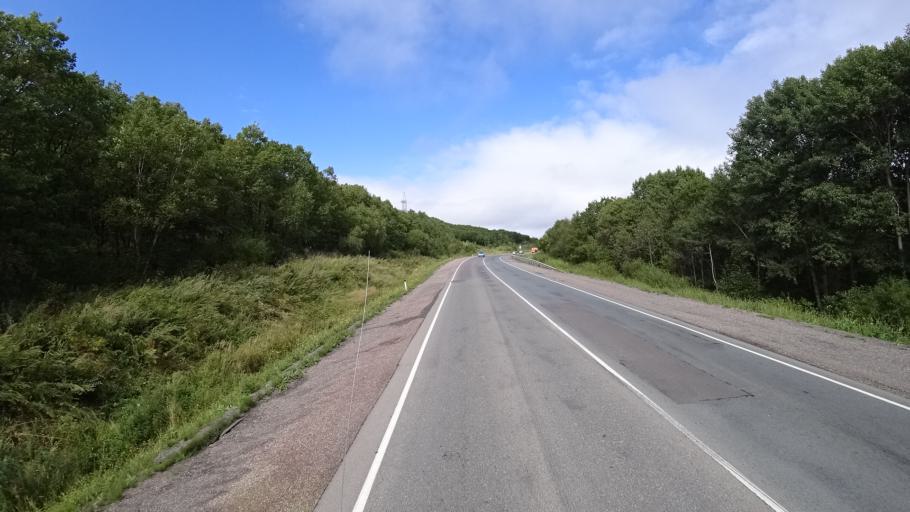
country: RU
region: Primorskiy
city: Lyalichi
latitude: 44.1193
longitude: 132.4196
